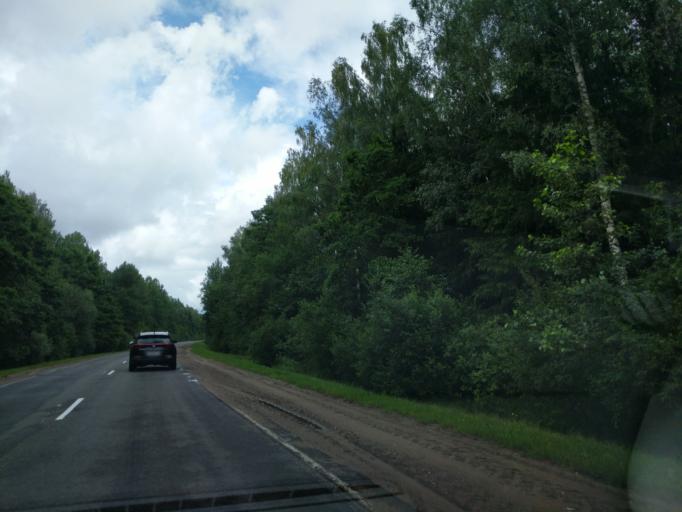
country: BY
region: Minsk
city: Il'ya
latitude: 54.4145
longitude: 27.2638
